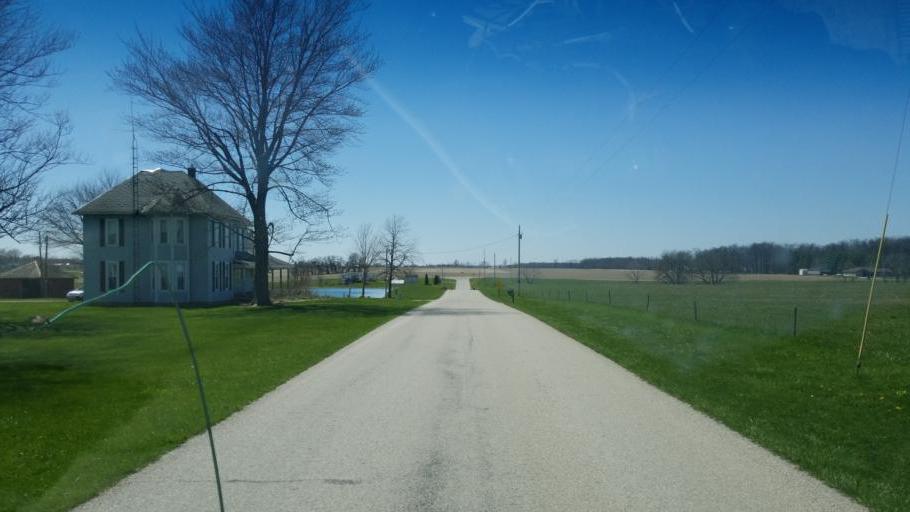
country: US
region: Ohio
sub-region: Huron County
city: Willard
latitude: 41.0838
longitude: -82.8285
